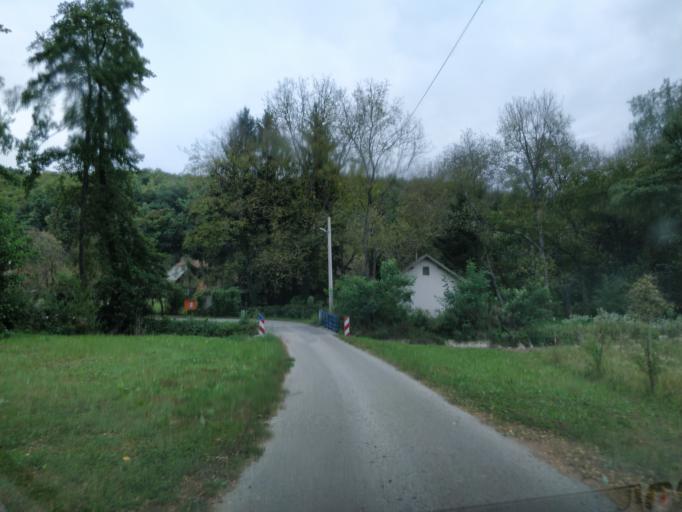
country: HR
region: Krapinsko-Zagorska
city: Oroslavje
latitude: 45.9402
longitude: 15.9179
